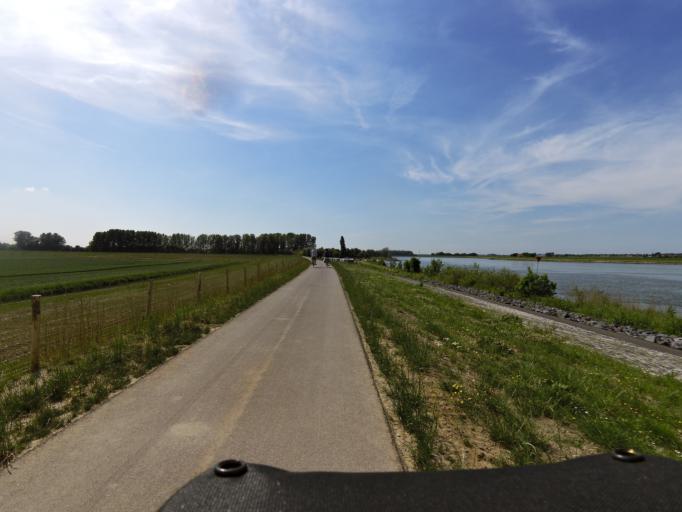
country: NL
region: South Holland
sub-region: Gemeente Spijkenisse
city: Spijkenisse
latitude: 51.8025
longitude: 4.2832
